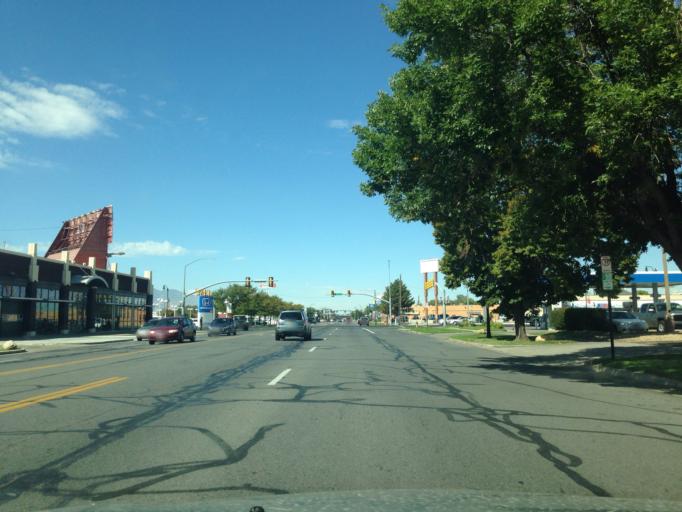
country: US
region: Utah
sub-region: Salt Lake County
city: Salt Lake City
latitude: 40.7498
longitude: -111.8870
